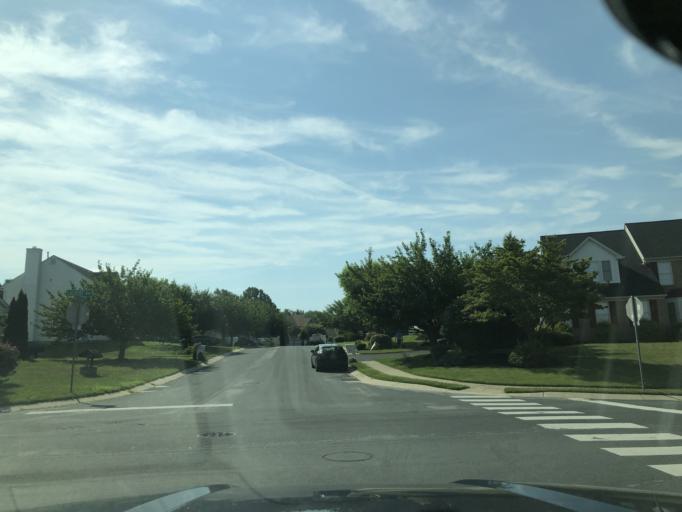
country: US
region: Maryland
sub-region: Carroll County
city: Eldersburg
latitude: 39.4118
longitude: -76.9665
